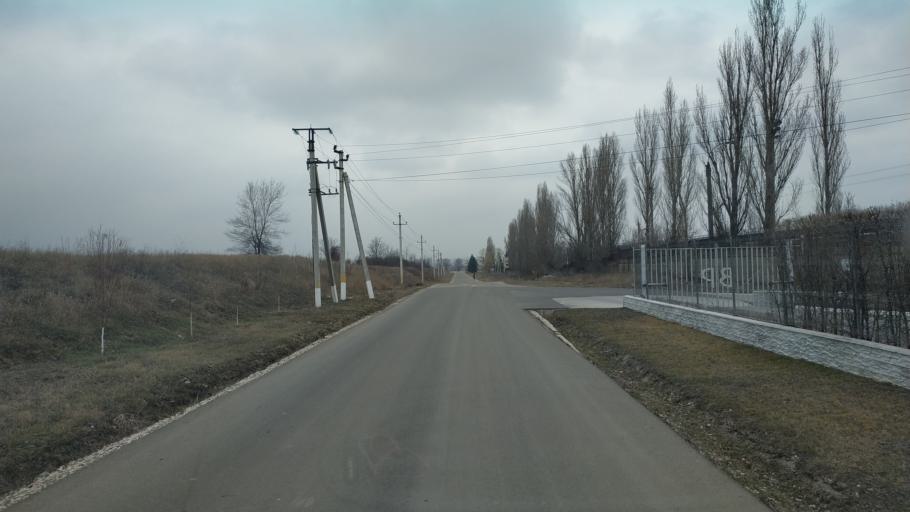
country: MD
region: Chisinau
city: Singera
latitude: 46.9097
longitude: 29.0072
